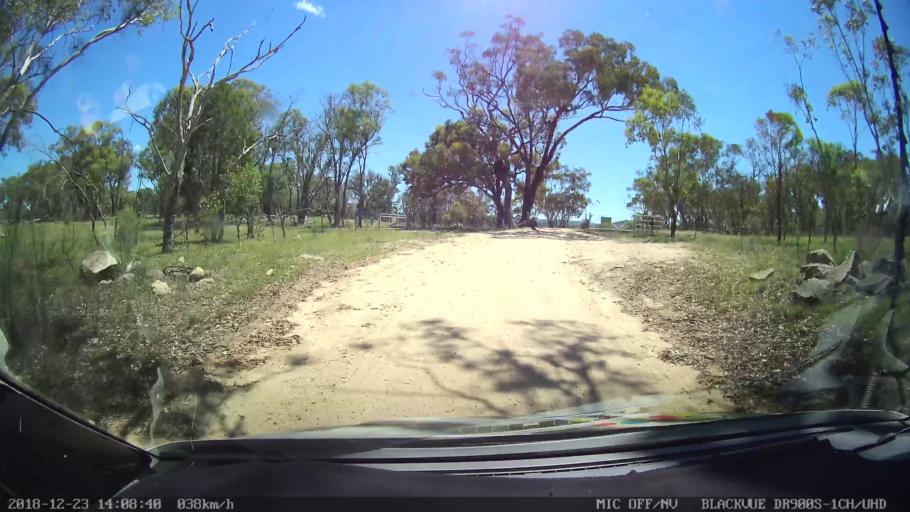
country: AU
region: New South Wales
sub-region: Tamworth Municipality
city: Manilla
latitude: -30.6429
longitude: 151.0665
